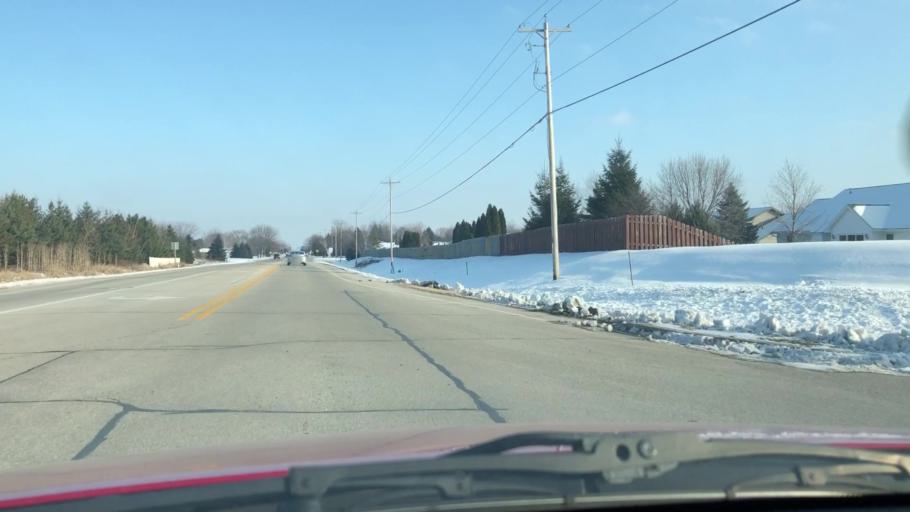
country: US
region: Wisconsin
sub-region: Outagamie County
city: Appleton
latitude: 44.3163
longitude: -88.4031
